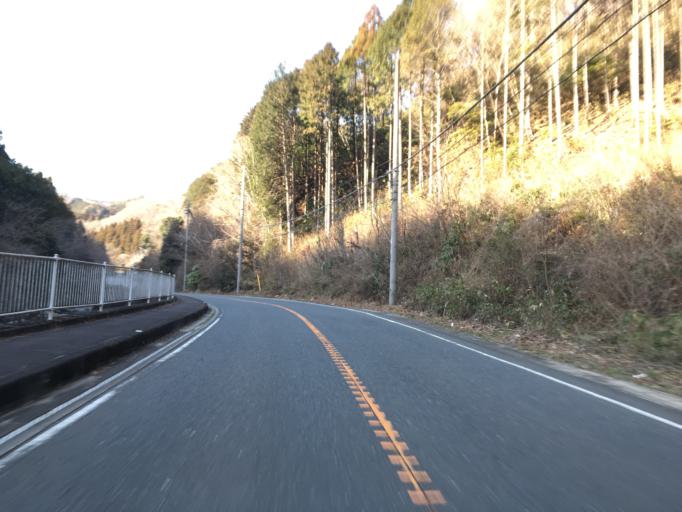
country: JP
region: Ibaraki
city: Takahagi
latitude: 36.7250
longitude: 140.6352
